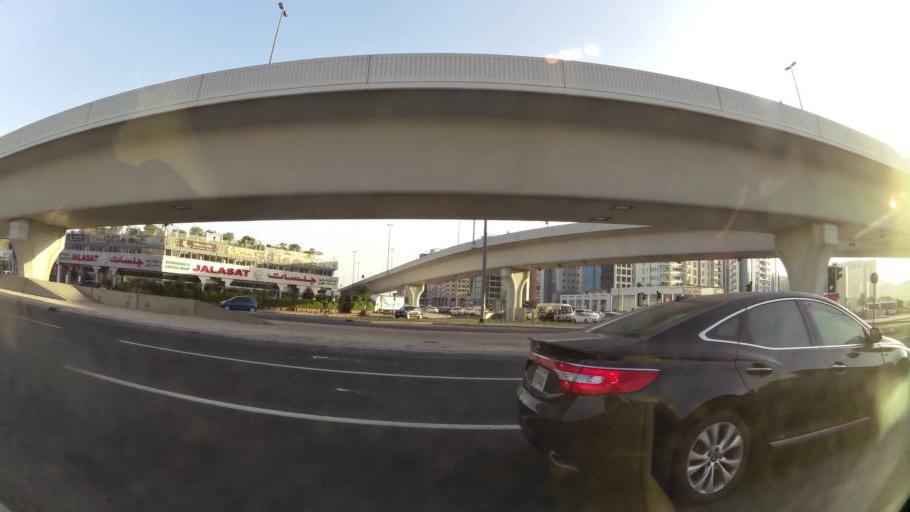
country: AE
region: Ash Shariqah
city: Sharjah
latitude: 25.2559
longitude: 55.3378
